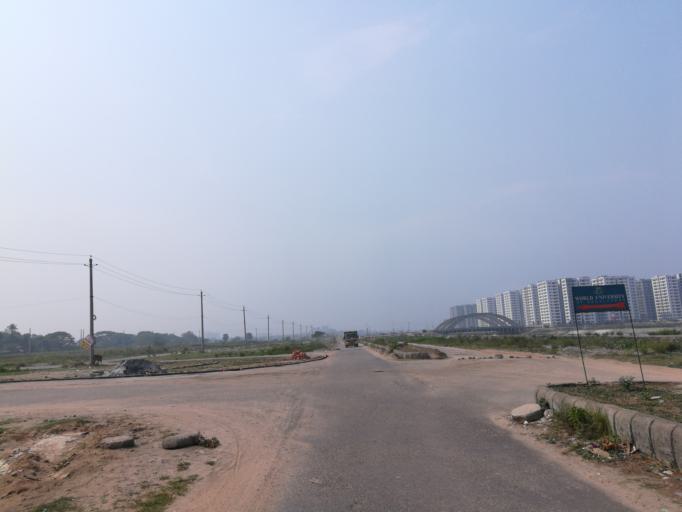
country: BD
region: Dhaka
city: Tungi
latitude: 23.8618
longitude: 90.3600
